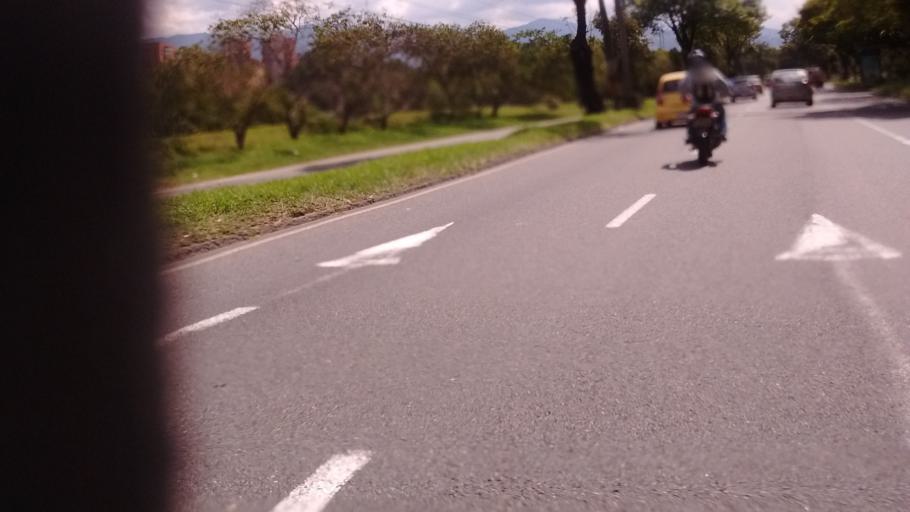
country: CO
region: Antioquia
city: Itagui
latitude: 6.1979
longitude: -75.5810
